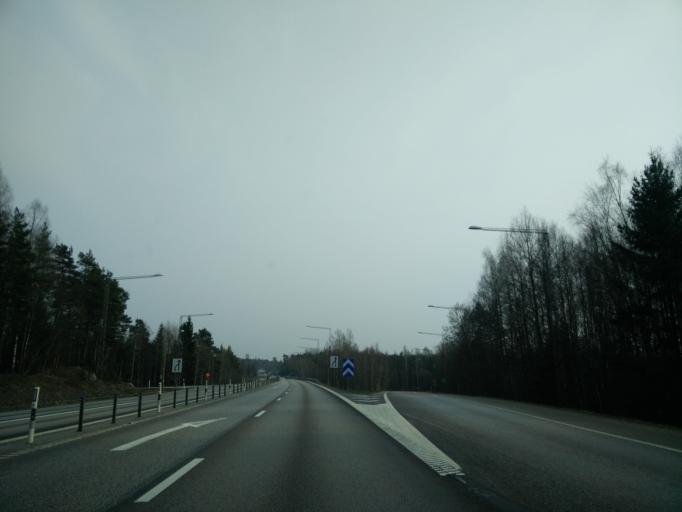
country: SE
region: Vaermland
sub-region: Hammaro Kommun
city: Skoghall
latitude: 59.3840
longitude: 13.4237
